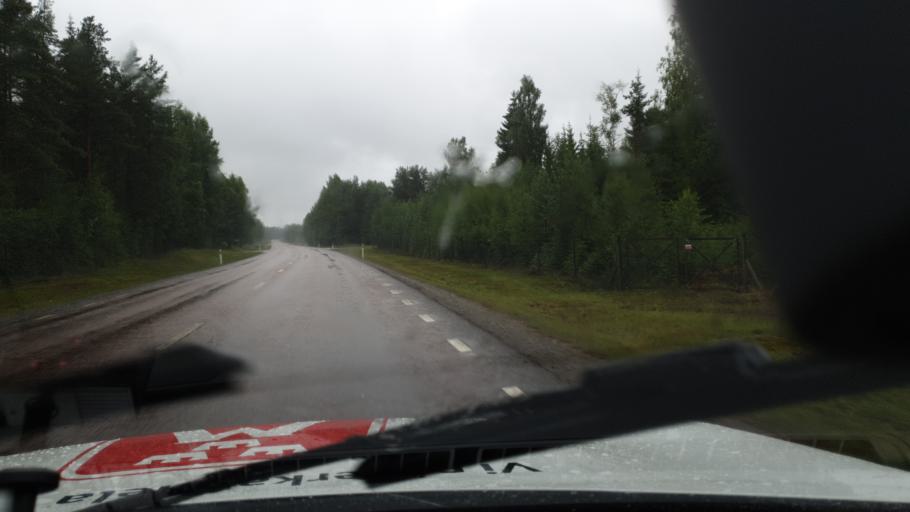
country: SE
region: Vaesterbotten
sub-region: Skelleftea Kommun
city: Burea
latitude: 64.6039
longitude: 21.2002
